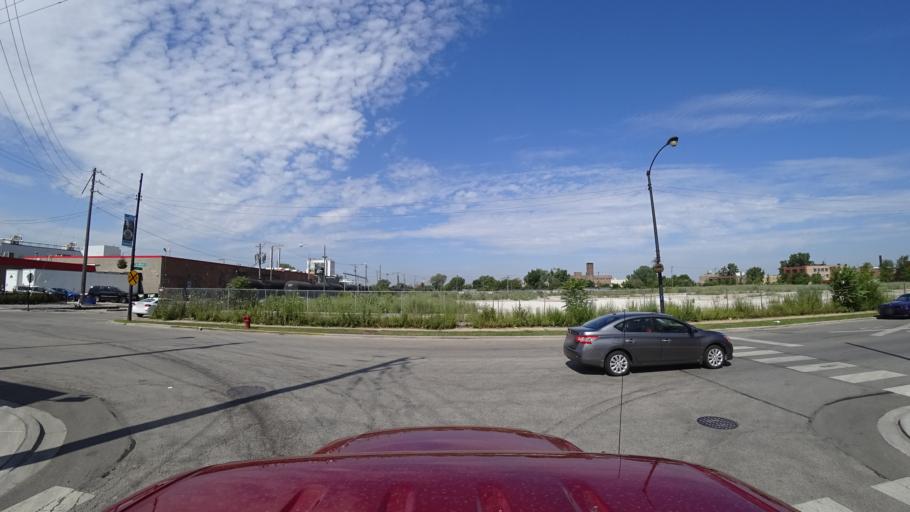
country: US
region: Illinois
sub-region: Cook County
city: Chicago
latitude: 41.8255
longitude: -87.6507
